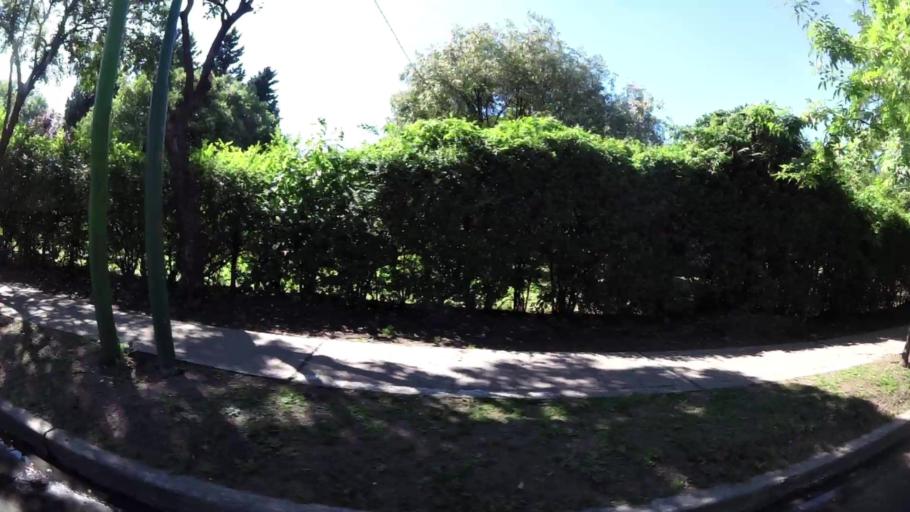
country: AR
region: Buenos Aires
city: Ituzaingo
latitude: -34.6204
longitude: -58.6555
